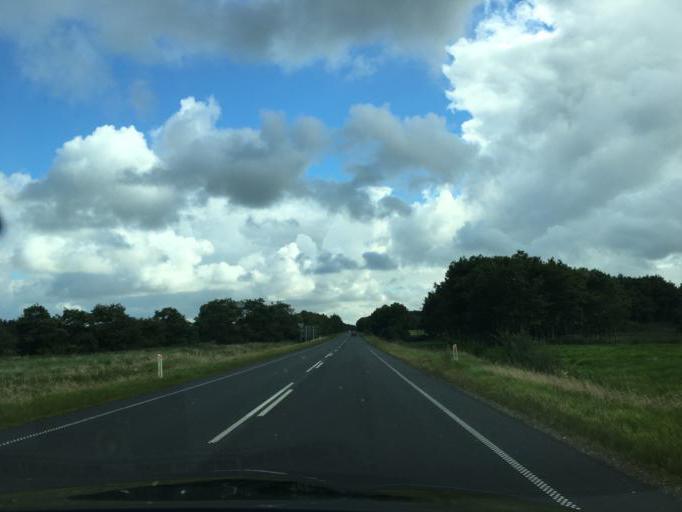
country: DK
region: South Denmark
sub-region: Varde Kommune
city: Olgod
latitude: 55.8033
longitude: 8.6289
